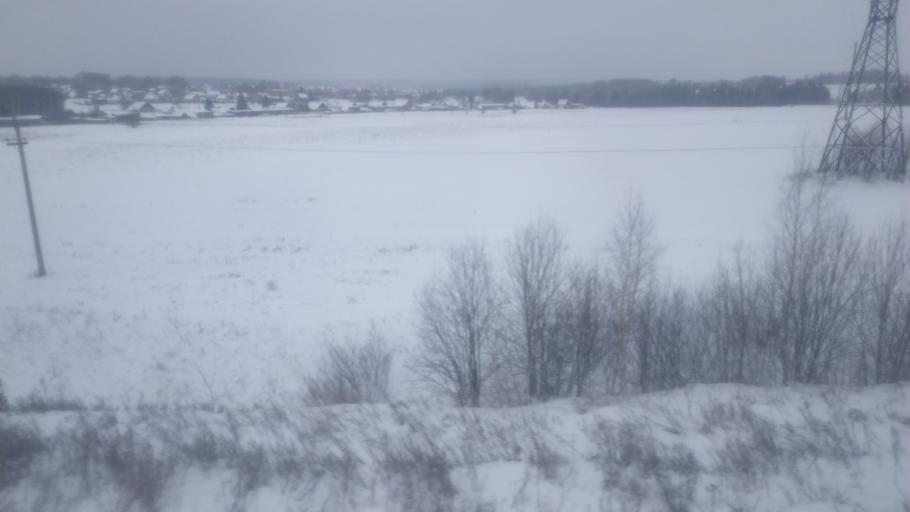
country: RU
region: Udmurtiya
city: Kiyasovo
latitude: 56.5027
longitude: 53.2268
